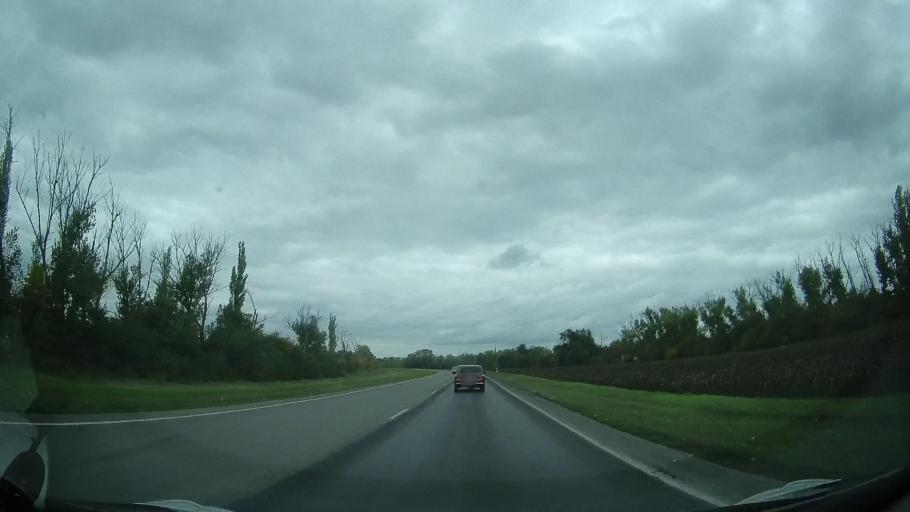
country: RU
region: Rostov
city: Yegorlykskaya
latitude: 46.5418
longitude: 40.7731
